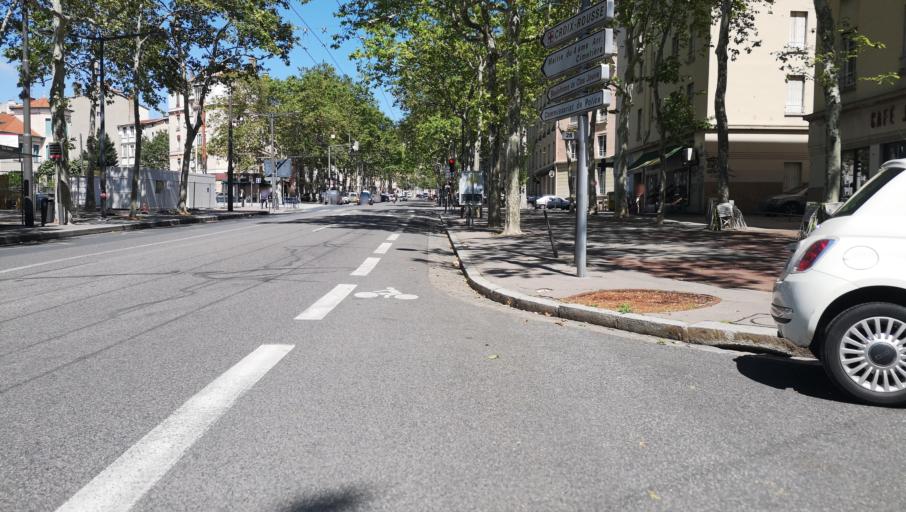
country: FR
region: Rhone-Alpes
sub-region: Departement du Rhone
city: Caluire-et-Cuire
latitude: 45.7727
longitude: 4.8206
